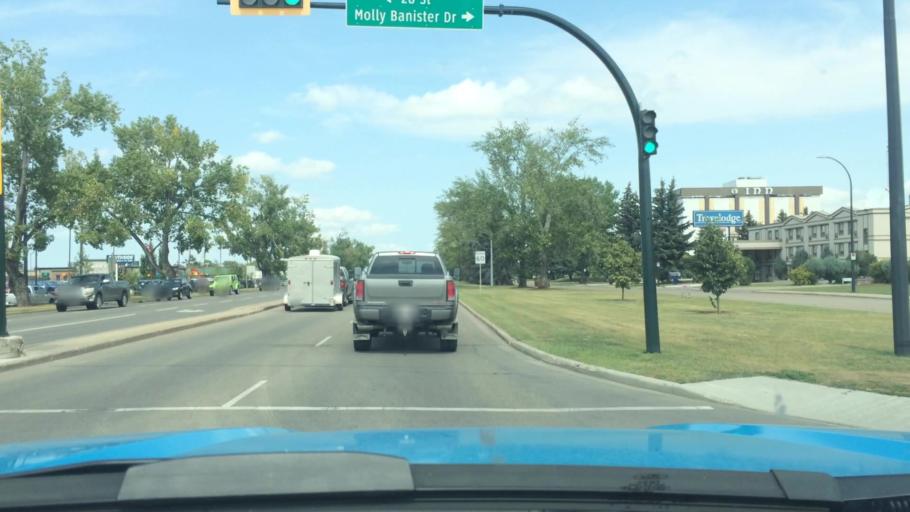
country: CA
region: Alberta
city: Red Deer
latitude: 52.2450
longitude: -113.8139
